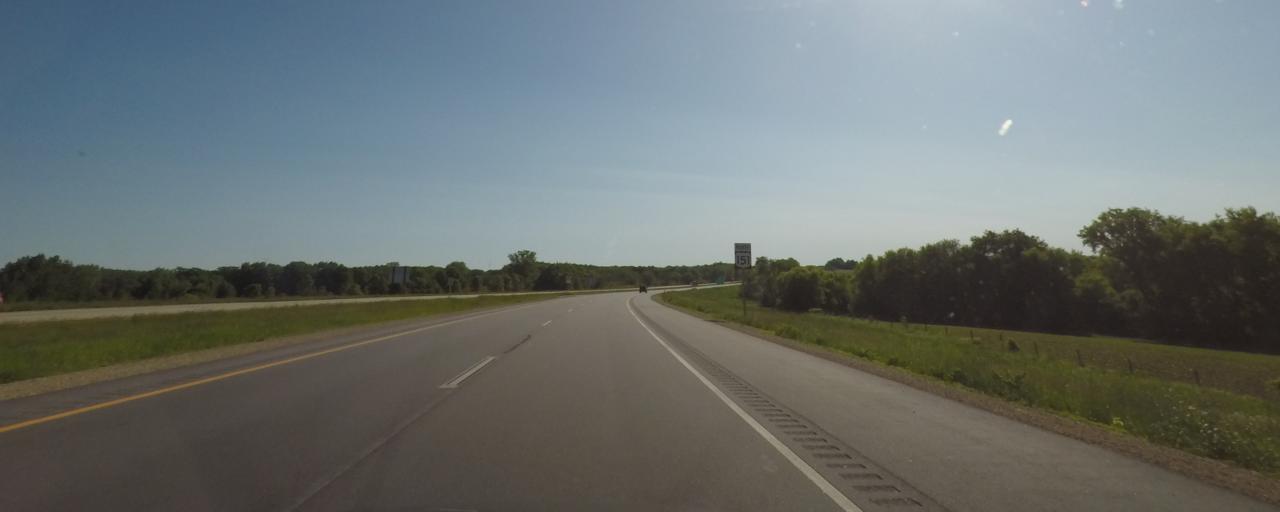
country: US
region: Wisconsin
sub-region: Columbia County
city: Columbus
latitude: 43.3531
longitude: -89.0255
